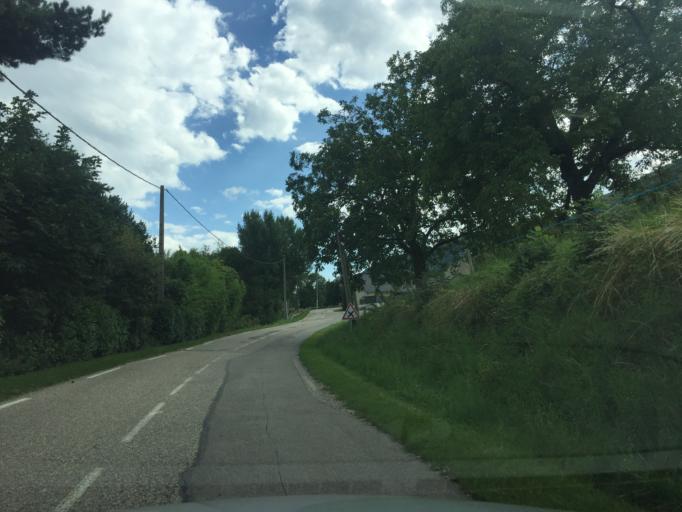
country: FR
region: Rhone-Alpes
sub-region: Departement de la Savoie
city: Vimines
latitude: 45.5703
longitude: 5.8456
